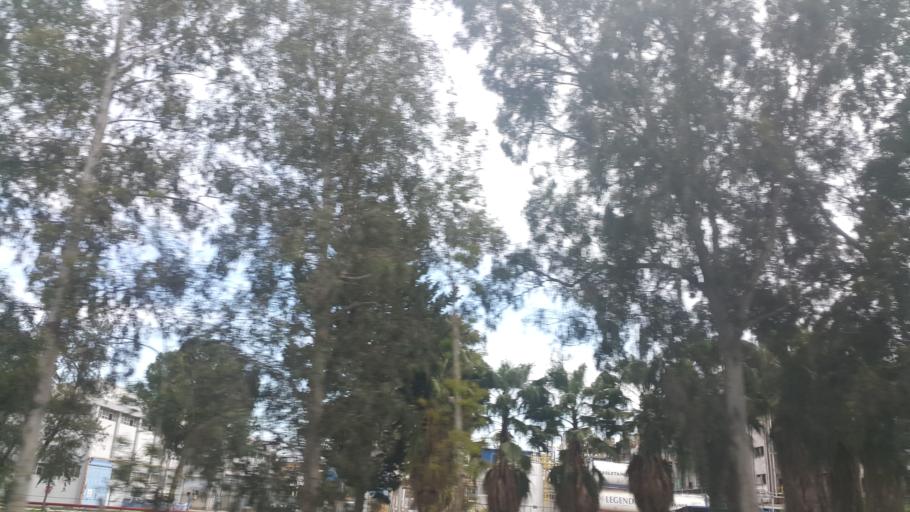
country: TR
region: Adana
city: Seyhan
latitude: 36.9935
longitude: 35.1995
